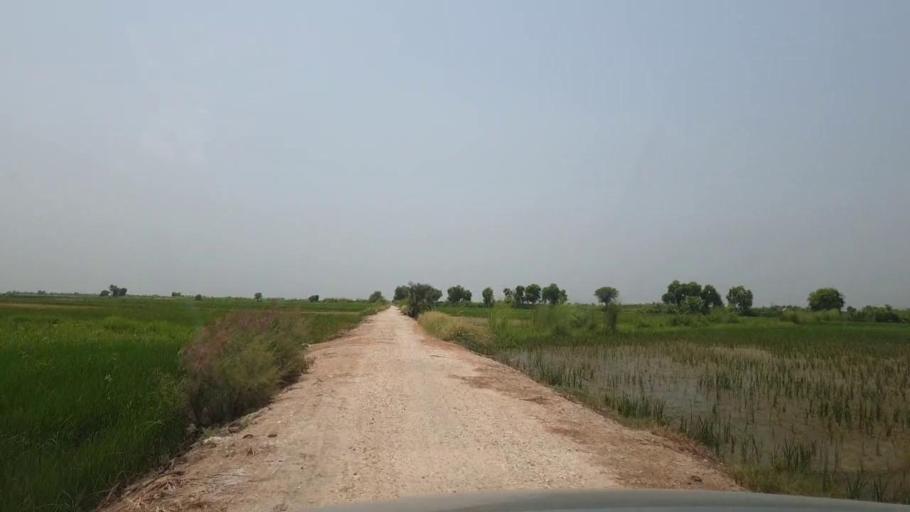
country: PK
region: Sindh
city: Garhi Yasin
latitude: 27.8721
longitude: 68.4919
